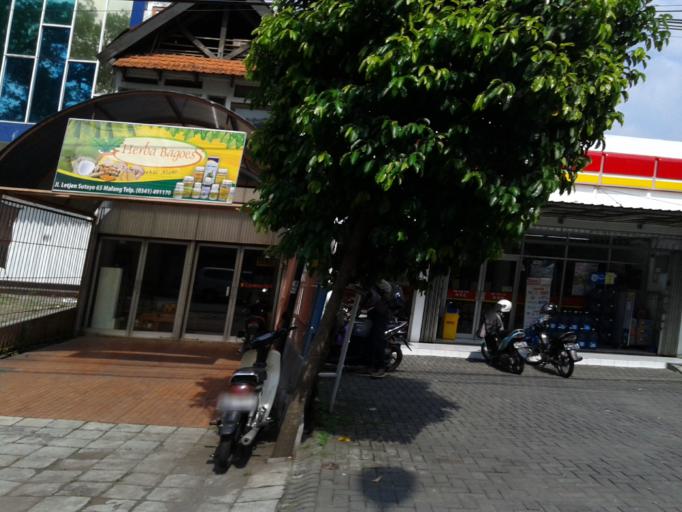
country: ID
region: East Java
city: Malang
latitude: -7.9640
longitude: 112.6353
